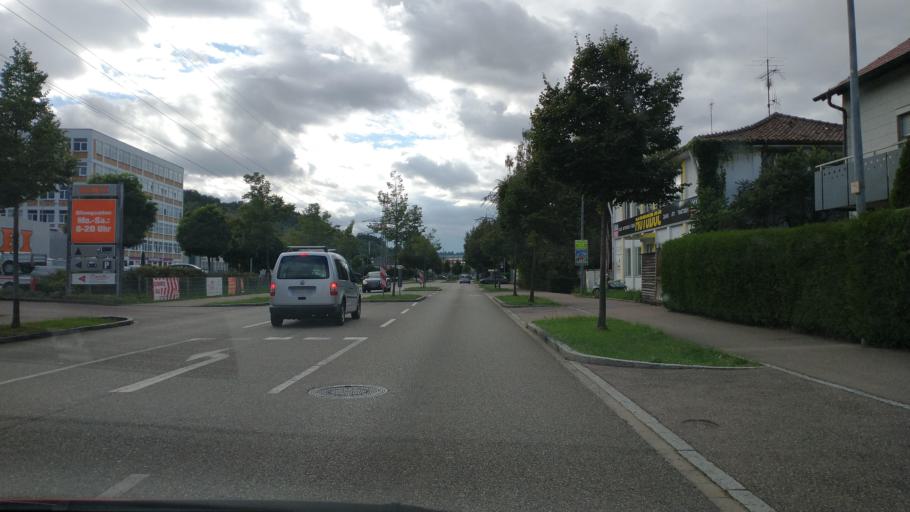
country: DE
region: Baden-Wuerttemberg
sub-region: Regierungsbezirk Stuttgart
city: Schwabisch Gmund
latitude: 48.8007
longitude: 9.8256
